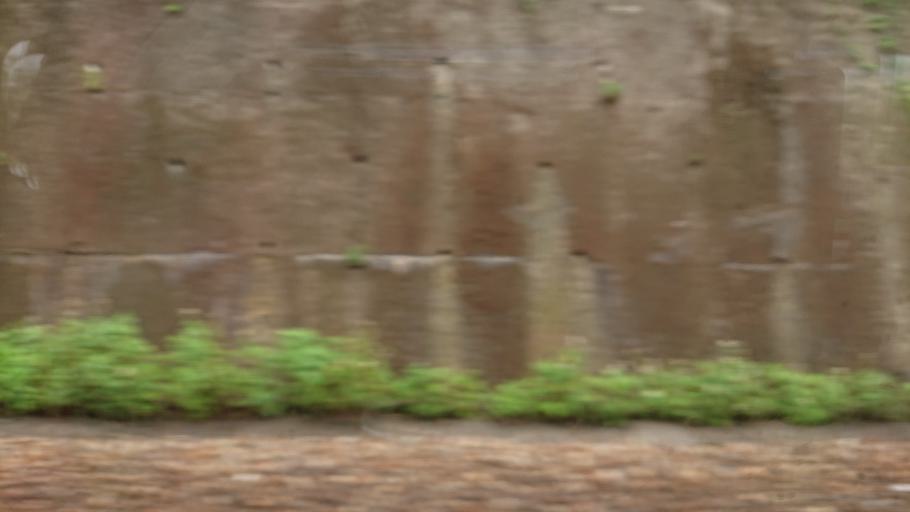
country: TW
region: Taiwan
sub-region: Keelung
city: Keelung
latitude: 24.9538
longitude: 121.9149
